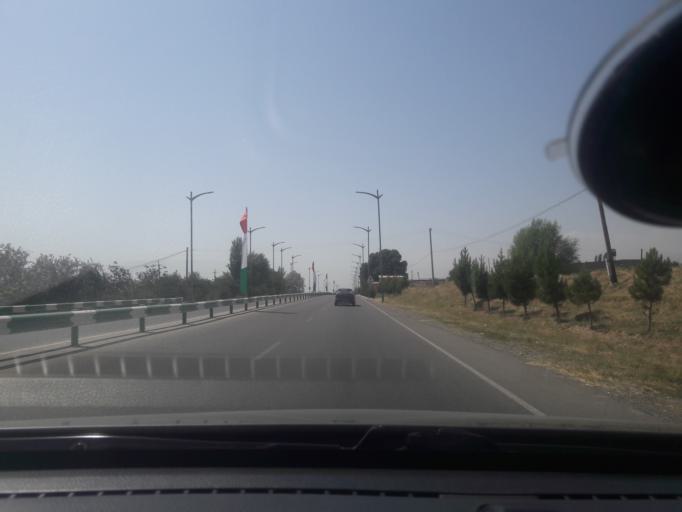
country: TJ
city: Shahrinav
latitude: 38.5612
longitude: 68.4408
